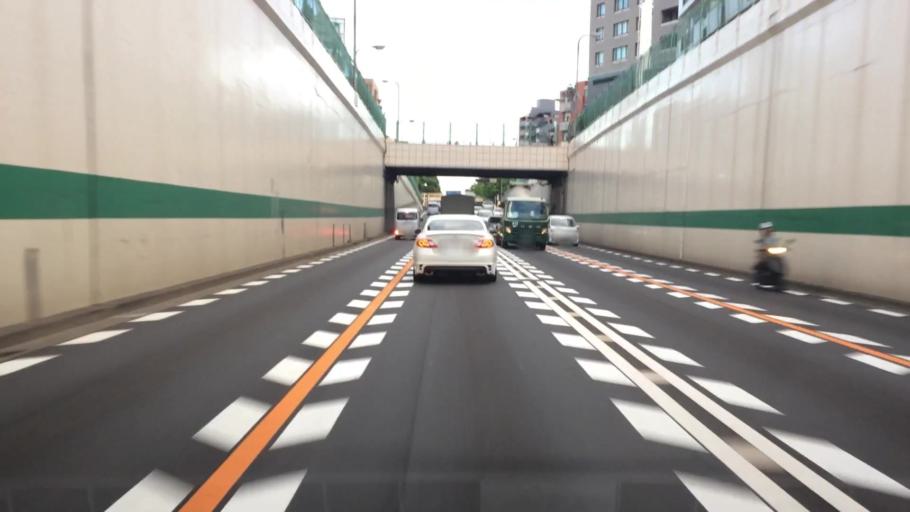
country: JP
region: Tokyo
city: Tokyo
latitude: 35.7193
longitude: 139.6538
